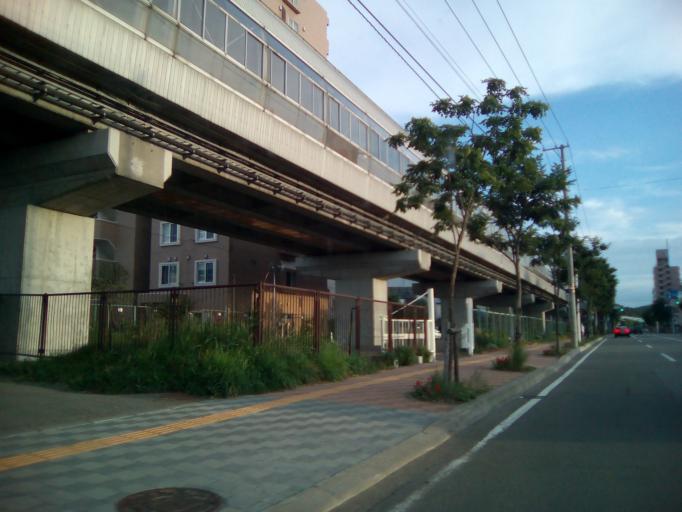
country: JP
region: Hokkaido
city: Sapporo
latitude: 43.0093
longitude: 141.3654
